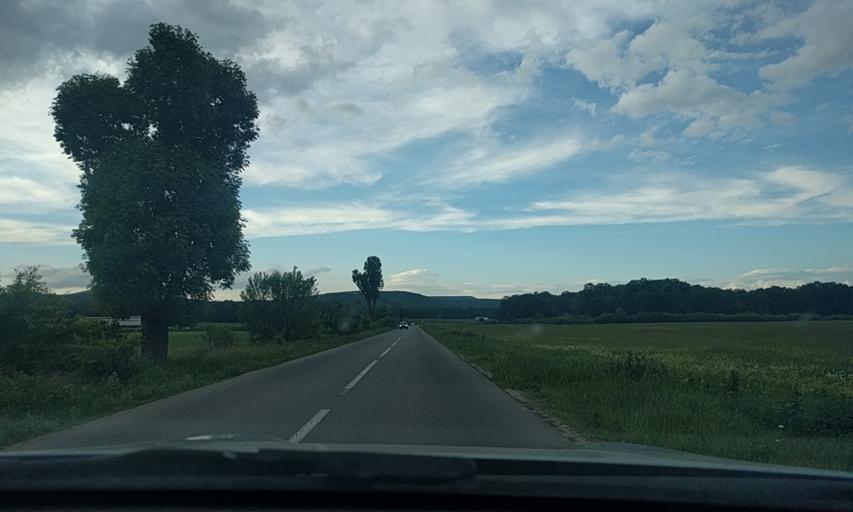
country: RO
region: Brasov
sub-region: Comuna Harman
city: Harman
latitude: 45.7418
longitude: 25.7040
